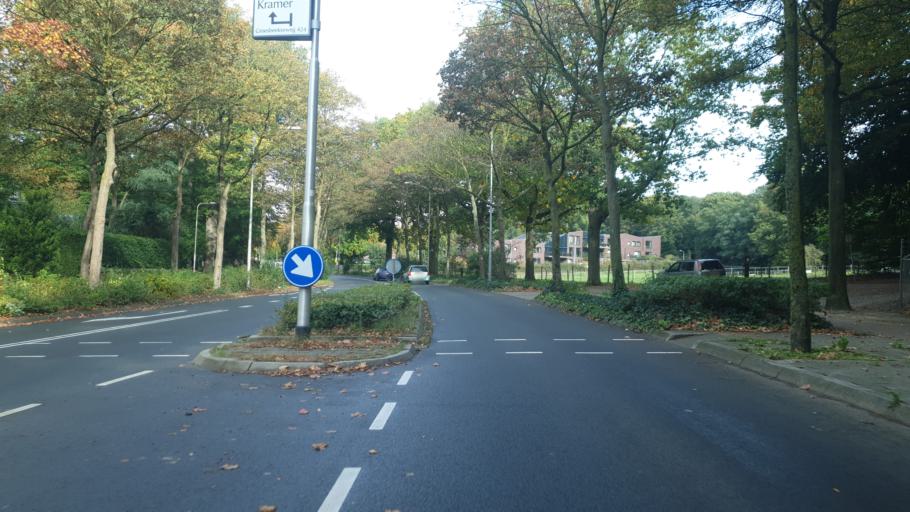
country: NL
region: Gelderland
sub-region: Gemeente Nijmegen
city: Nijmegen
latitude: 51.8229
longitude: 5.8804
